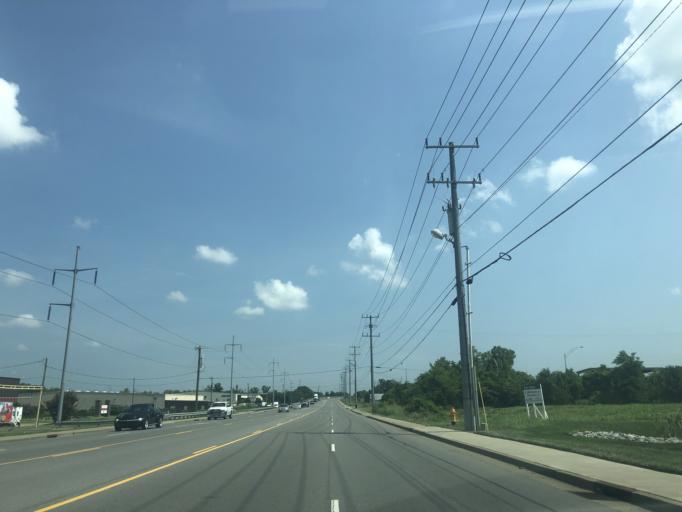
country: US
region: Tennessee
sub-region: Rutherford County
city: La Vergne
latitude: 36.0157
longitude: -86.5934
